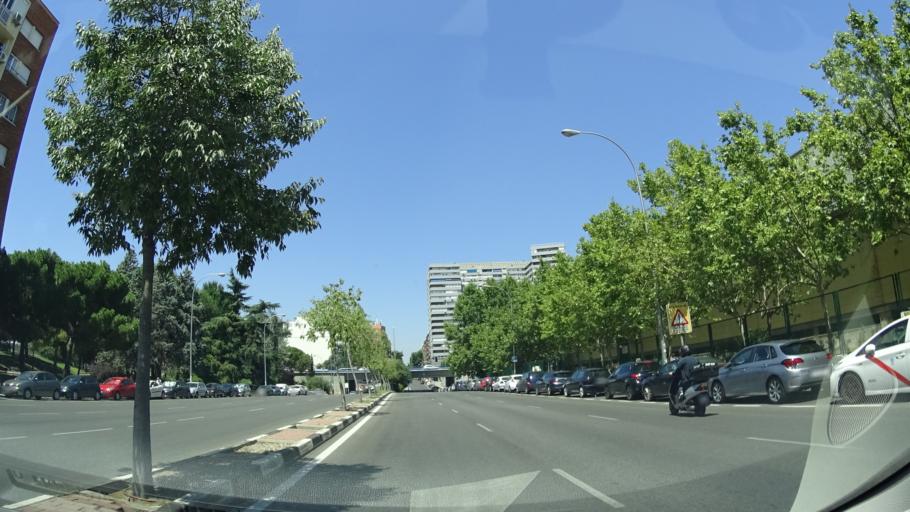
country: ES
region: Madrid
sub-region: Provincia de Madrid
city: Usera
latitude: 40.3924
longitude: -3.7044
